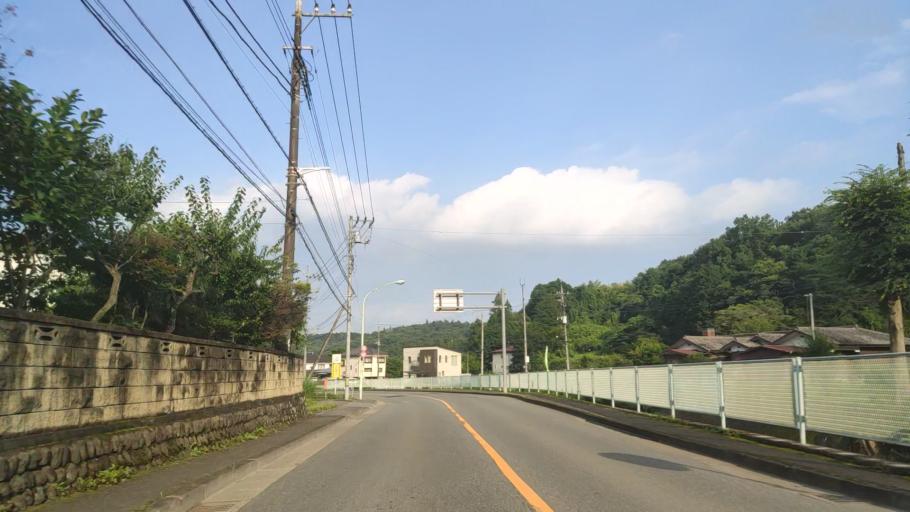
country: JP
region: Saitama
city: Hanno
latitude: 35.8221
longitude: 139.2775
